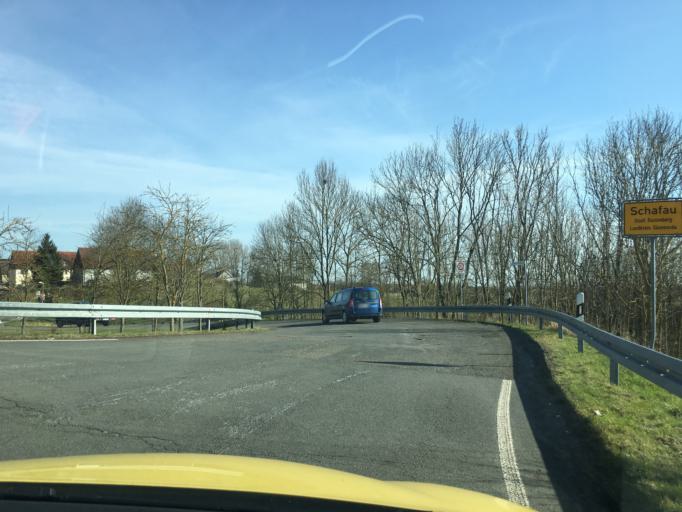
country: DE
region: Thuringia
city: Rastenberg
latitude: 51.1941
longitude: 11.3857
